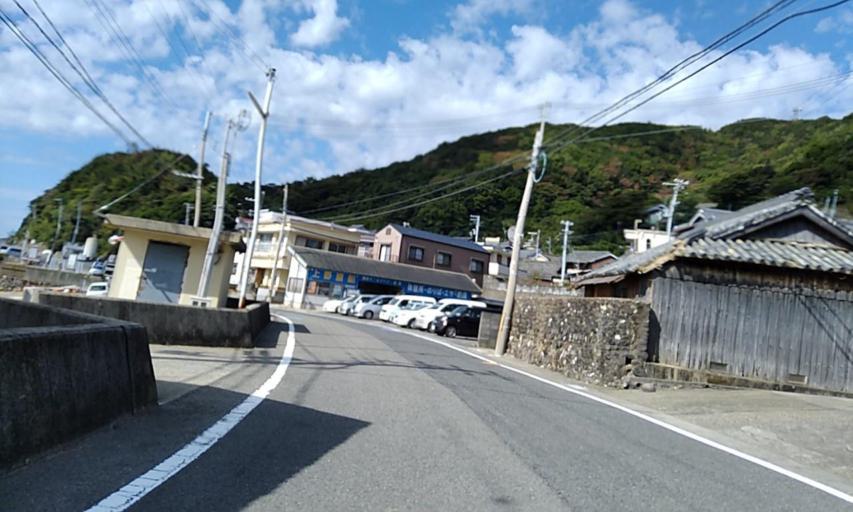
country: JP
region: Wakayama
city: Gobo
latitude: 33.9701
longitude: 135.0848
